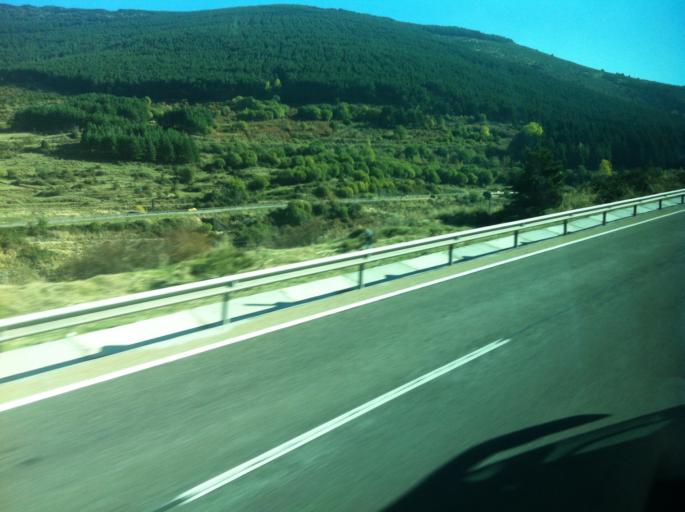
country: ES
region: Madrid
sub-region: Provincia de Madrid
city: Somosierra
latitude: 41.1710
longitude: -3.5823
